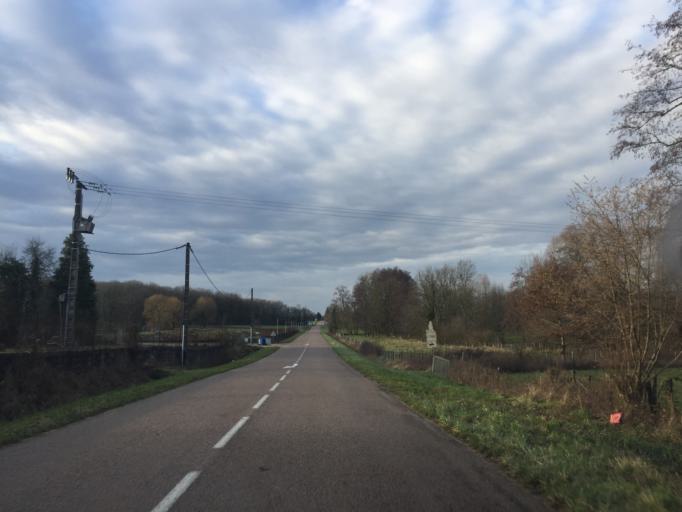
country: FR
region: Franche-Comte
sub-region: Departement du Jura
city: Arbois
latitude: 46.9274
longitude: 5.6874
